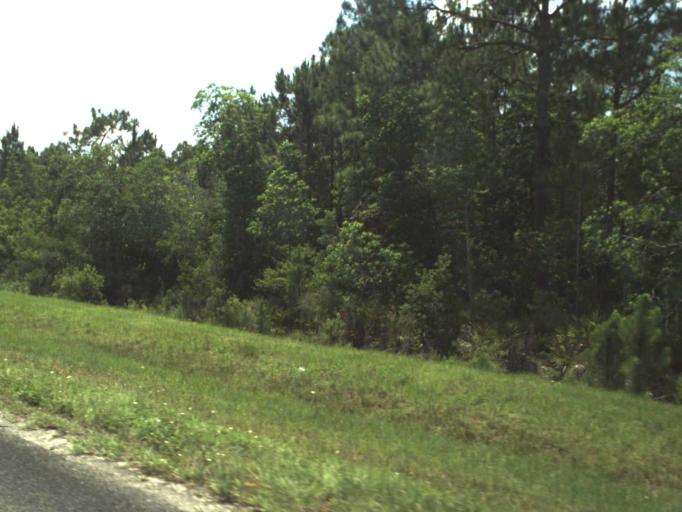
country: US
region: Florida
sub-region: Volusia County
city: Lake Helen
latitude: 29.0283
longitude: -81.1839
